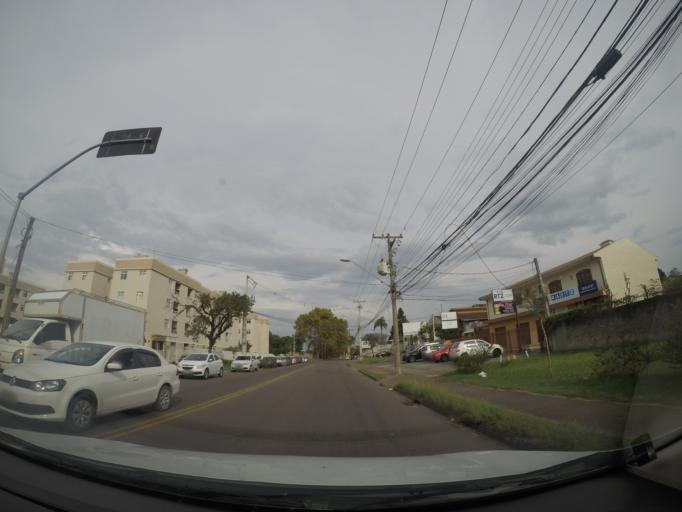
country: BR
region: Parana
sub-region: Sao Jose Dos Pinhais
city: Sao Jose dos Pinhais
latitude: -25.4895
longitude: -49.2229
